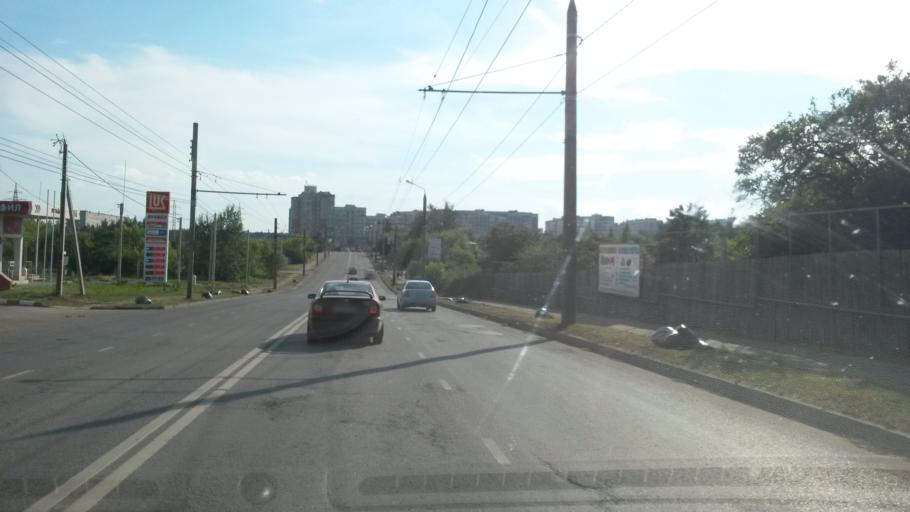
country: RU
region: Ivanovo
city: Kokhma
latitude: 56.9640
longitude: 41.0350
